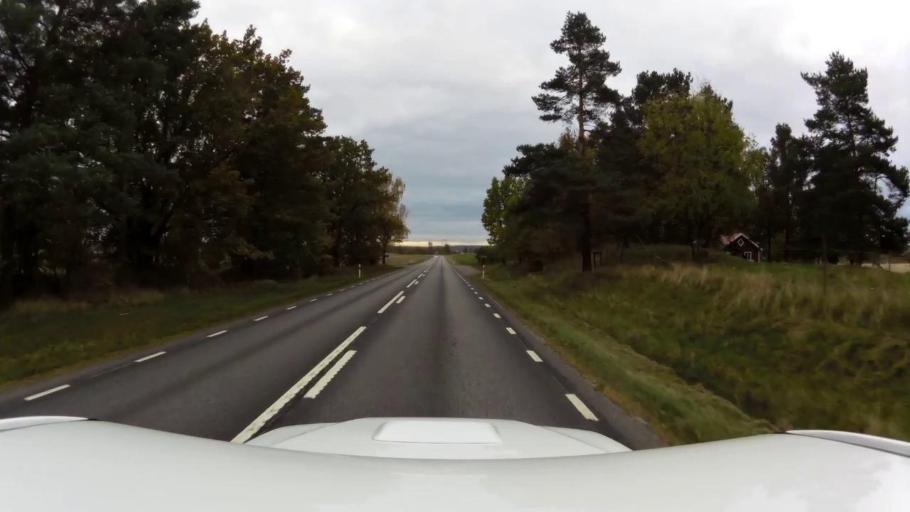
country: SE
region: OEstergoetland
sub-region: Linkopings Kommun
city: Ljungsbro
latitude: 58.5087
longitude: 15.4478
